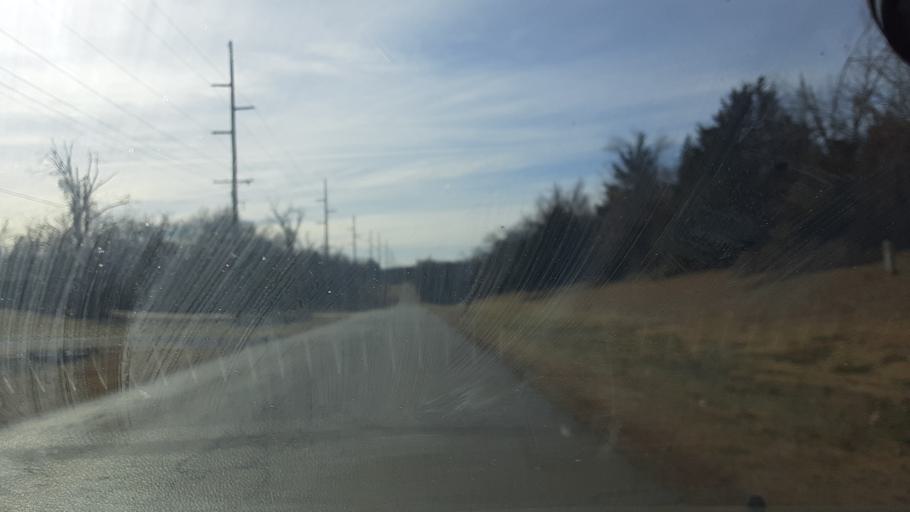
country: US
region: Oklahoma
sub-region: Logan County
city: Guthrie
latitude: 35.8898
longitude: -97.4075
